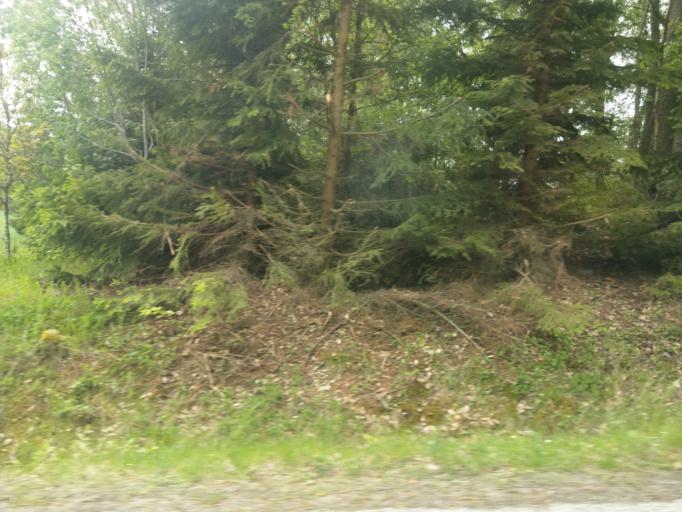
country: SE
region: Stockholm
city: Stenhamra
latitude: 59.4148
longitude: 17.6163
